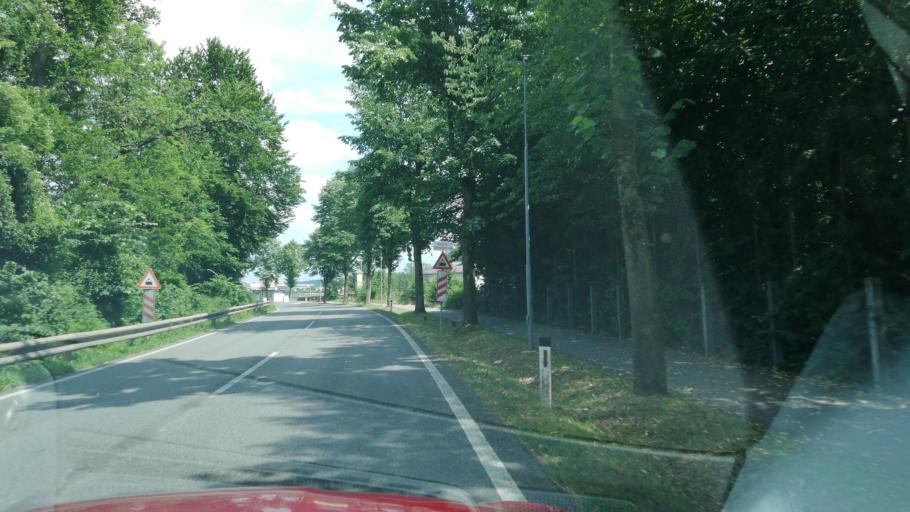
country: AT
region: Upper Austria
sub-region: Politischer Bezirk Vocklabruck
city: Timelkam
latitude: 48.0018
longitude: 13.6216
